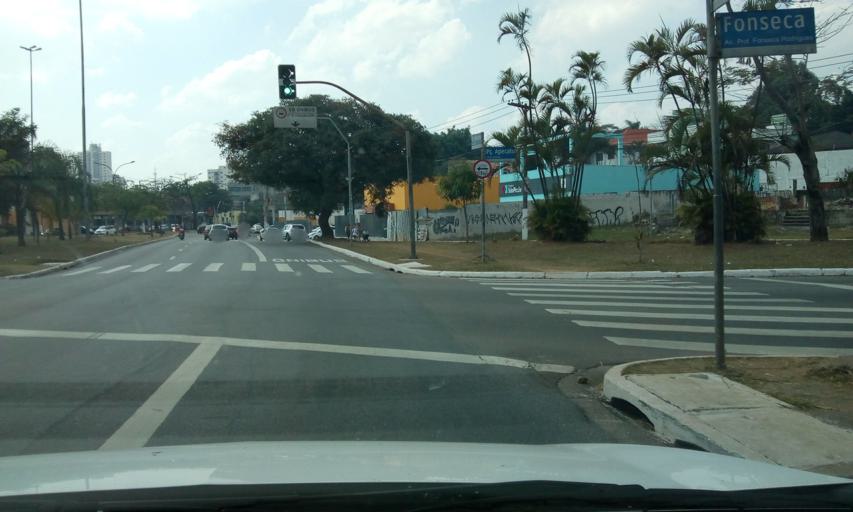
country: BR
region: Sao Paulo
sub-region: Osasco
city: Osasco
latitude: -23.5405
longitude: -46.7285
